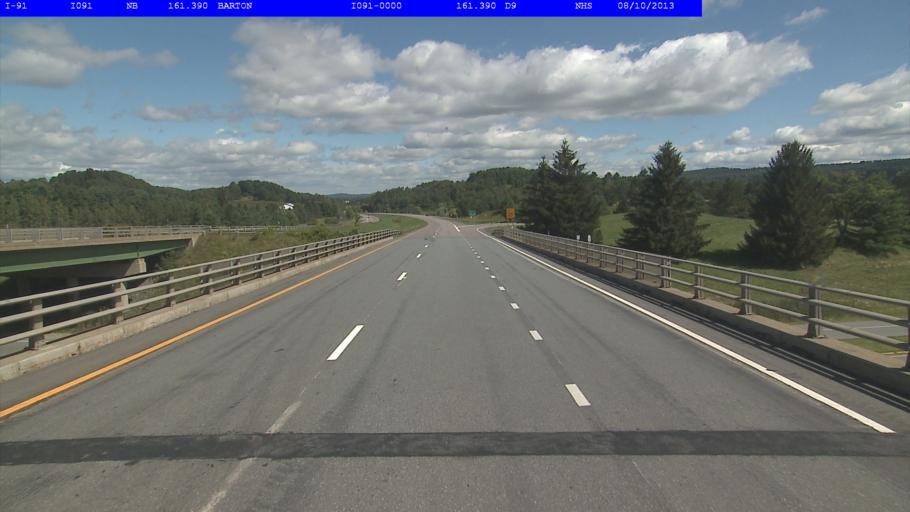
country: US
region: Vermont
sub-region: Orleans County
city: Newport
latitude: 44.8061
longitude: -72.2123
